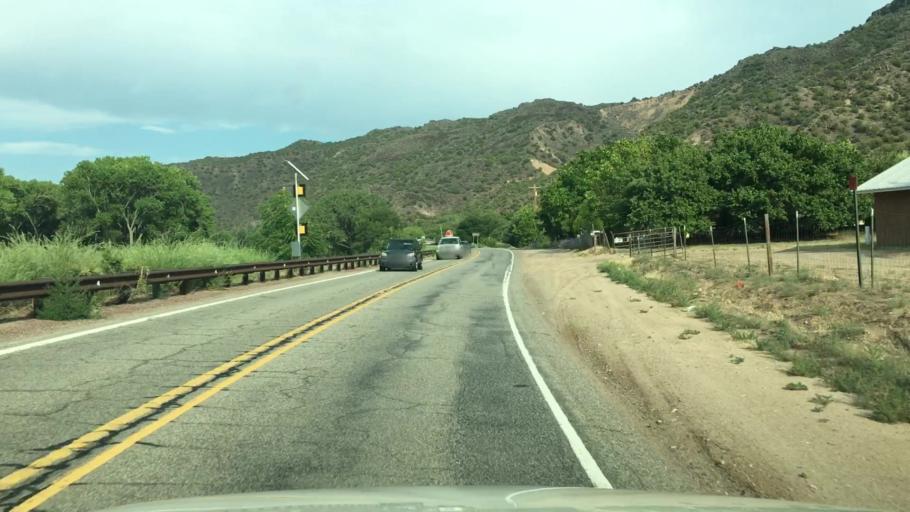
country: US
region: New Mexico
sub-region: Rio Arriba County
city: Ohkay Owingeh
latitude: 36.2096
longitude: -105.9543
